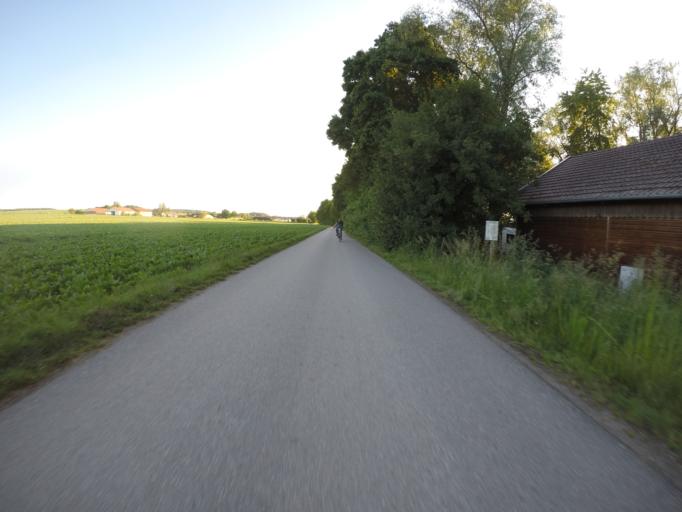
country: DE
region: Bavaria
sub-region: Lower Bavaria
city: Reisbach
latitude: 48.5640
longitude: 12.5977
